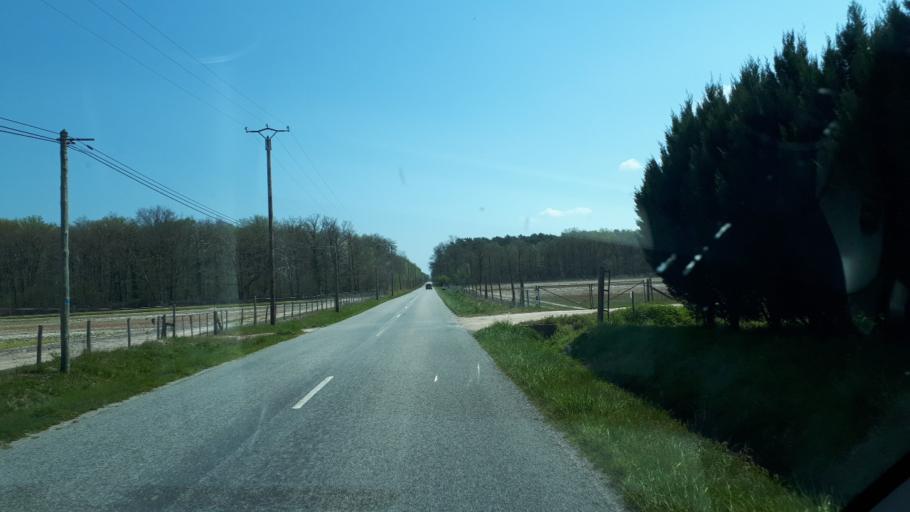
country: FR
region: Centre
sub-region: Departement du Loir-et-Cher
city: Theillay
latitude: 47.3137
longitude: 2.0920
